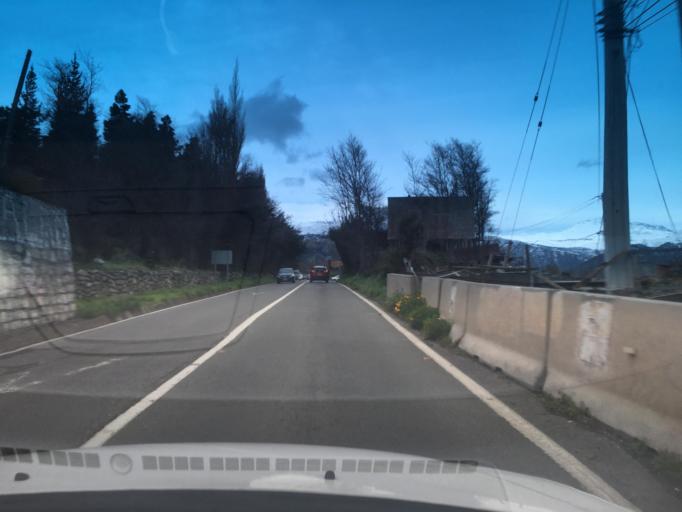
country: CL
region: Santiago Metropolitan
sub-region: Provincia de Cordillera
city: Puente Alto
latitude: -33.5788
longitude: -70.4182
